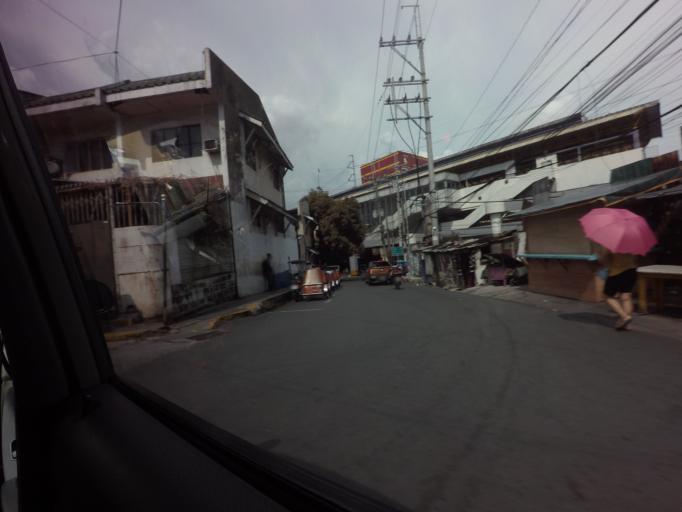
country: PH
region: Metro Manila
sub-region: San Juan
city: San Juan
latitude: 14.6041
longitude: 121.0163
